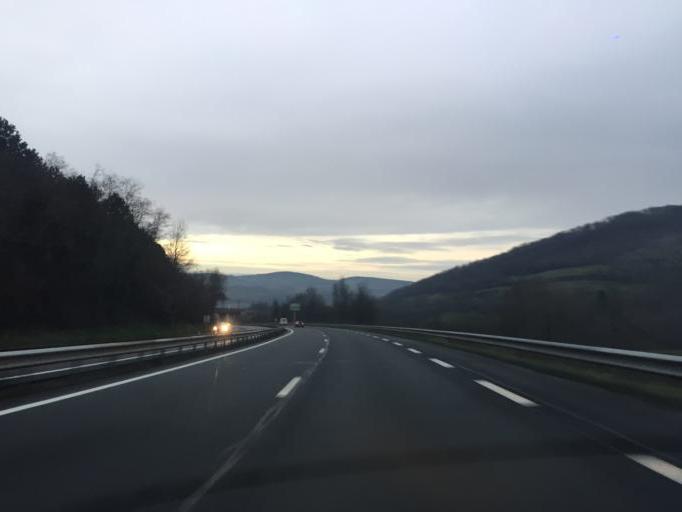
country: FR
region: Bourgogne
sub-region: Departement de Saone-et-Loire
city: Cluny
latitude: 46.3876
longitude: 4.6644
